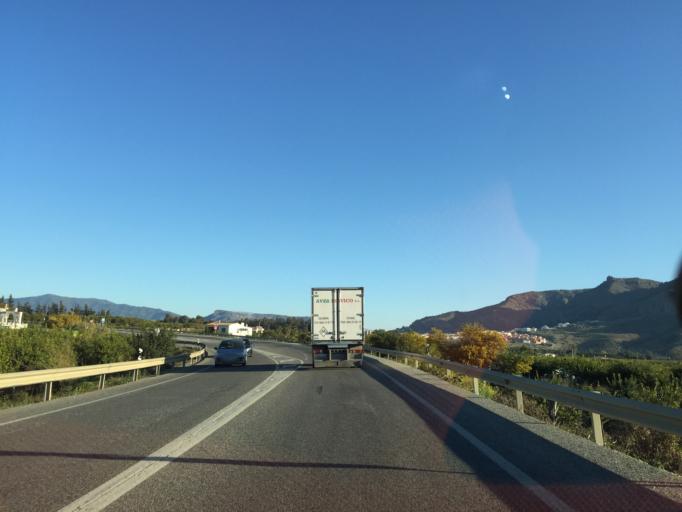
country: ES
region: Andalusia
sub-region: Provincia de Malaga
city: Pizarra
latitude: 36.7455
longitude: -4.7112
